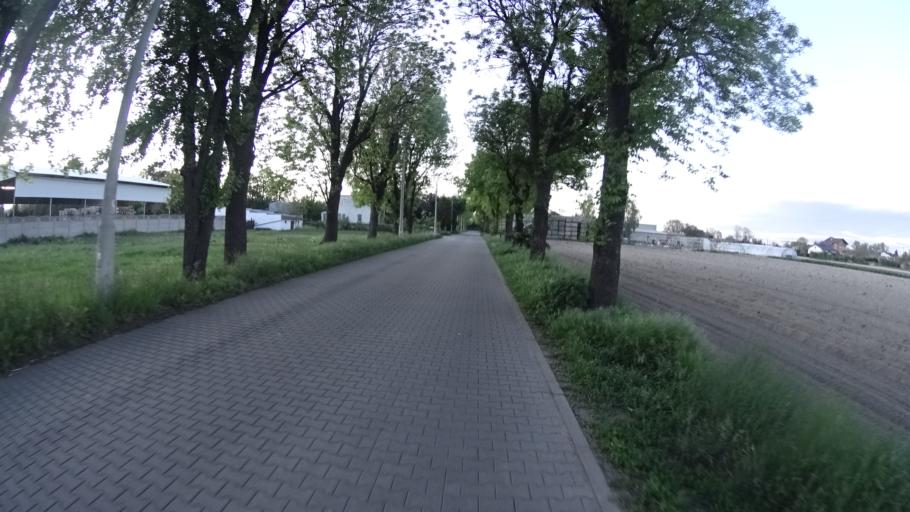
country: PL
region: Masovian Voivodeship
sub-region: Powiat warszawski zachodni
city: Ozarow Mazowiecki
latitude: 52.2093
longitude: 20.7557
